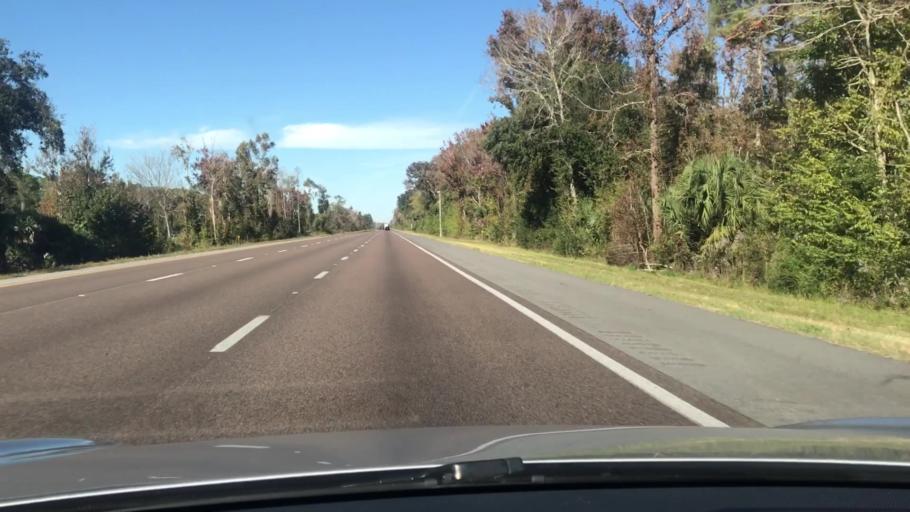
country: US
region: Florida
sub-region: Volusia County
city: Oak Hill
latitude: 28.8811
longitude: -80.9232
